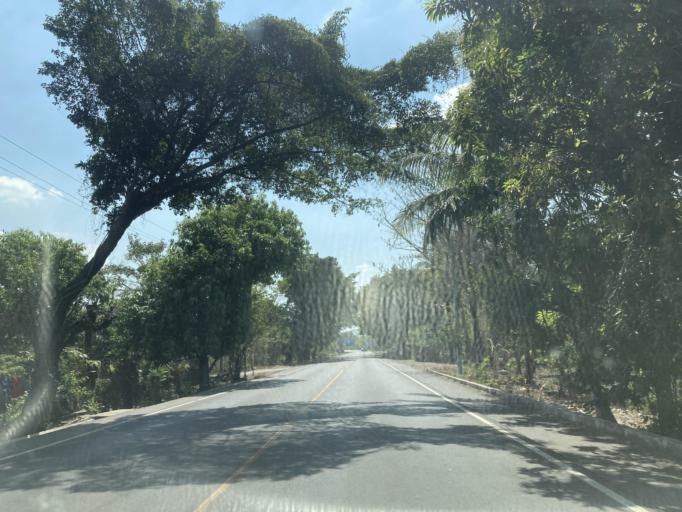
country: GT
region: Escuintla
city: Guanagazapa
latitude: 14.2034
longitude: -90.7139
